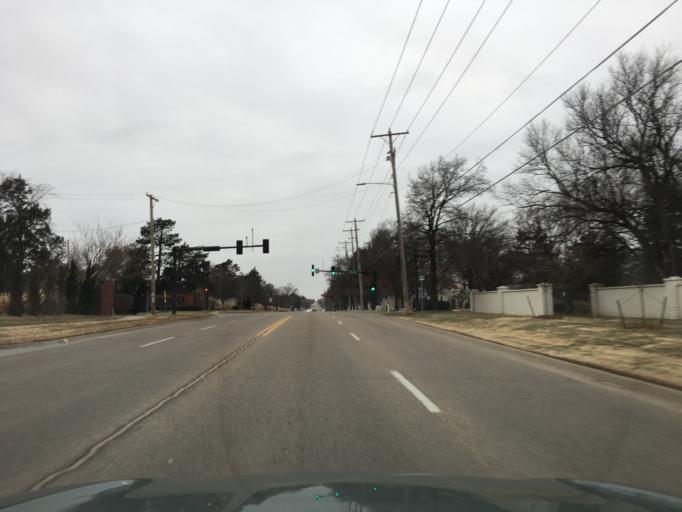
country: US
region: Kansas
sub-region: Sedgwick County
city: Bellaire
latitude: 37.7085
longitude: -97.2319
